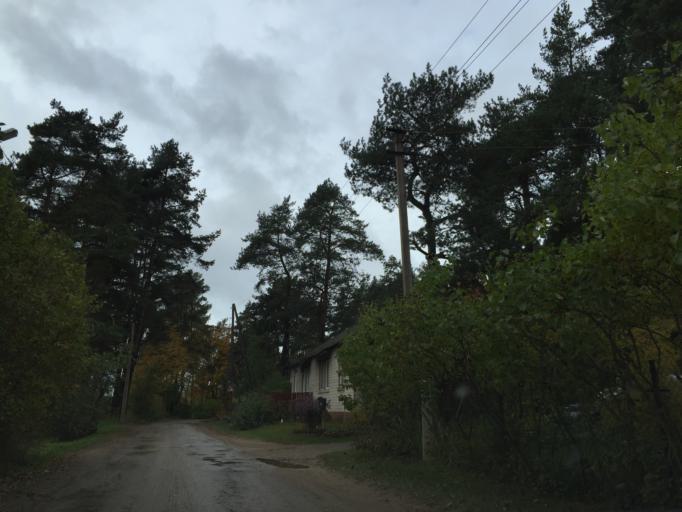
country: LV
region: Ogre
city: Ogre
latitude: 56.7961
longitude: 24.6444
